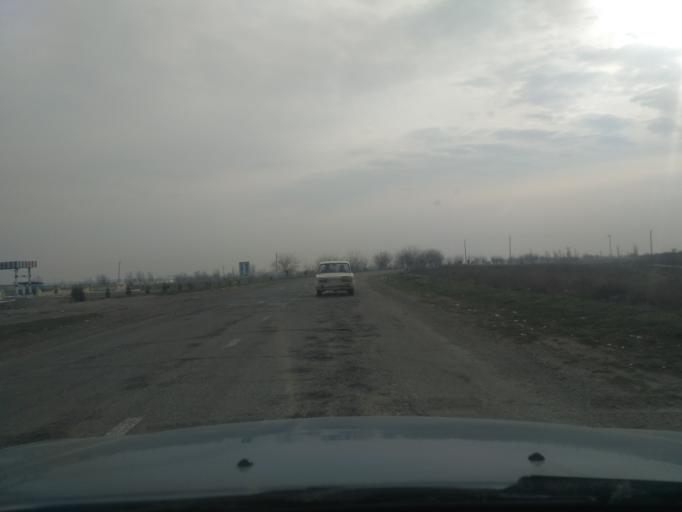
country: UZ
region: Sirdaryo
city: Sirdaryo
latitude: 40.8256
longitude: 68.6259
